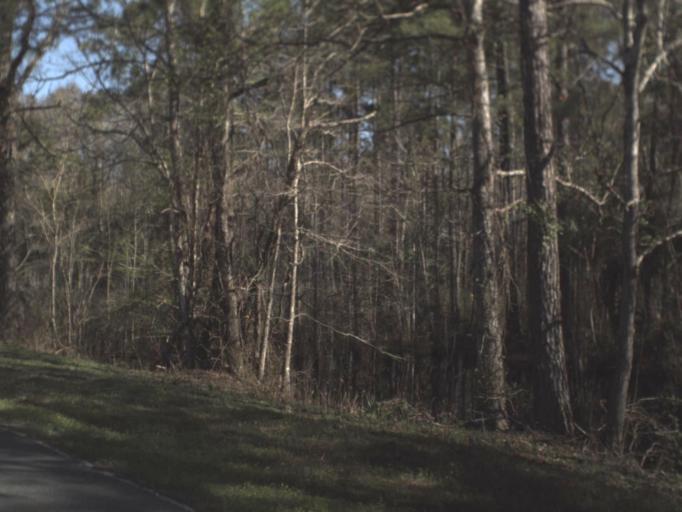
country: US
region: Florida
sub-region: Leon County
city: Woodville
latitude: 30.1796
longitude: -84.0116
